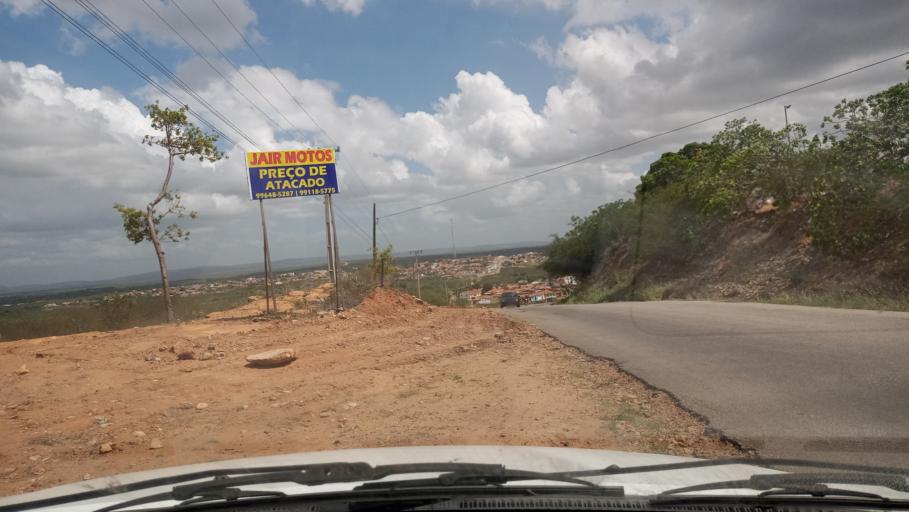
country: BR
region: Rio Grande do Norte
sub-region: Sao Paulo Do Potengi
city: Sao Paulo do Potengi
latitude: -5.9076
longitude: -35.7594
